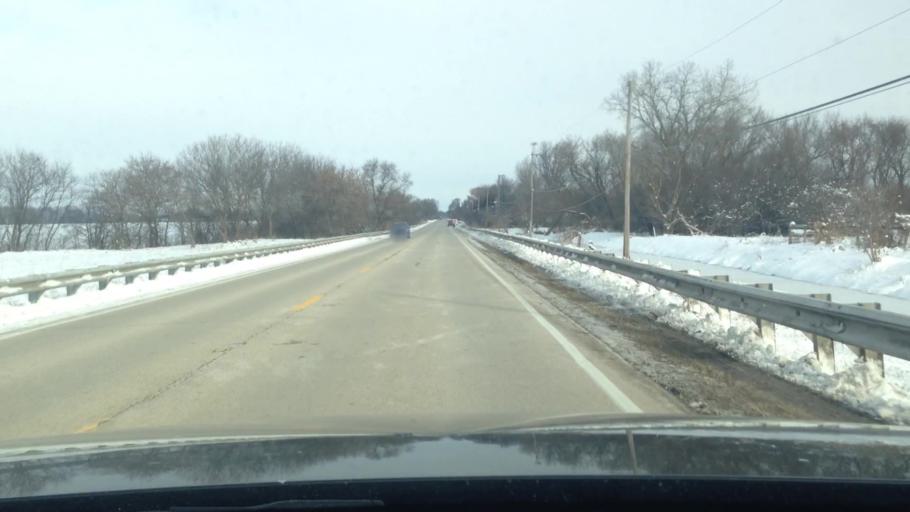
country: US
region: Illinois
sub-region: McHenry County
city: Woodstock
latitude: 42.3684
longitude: -88.4431
